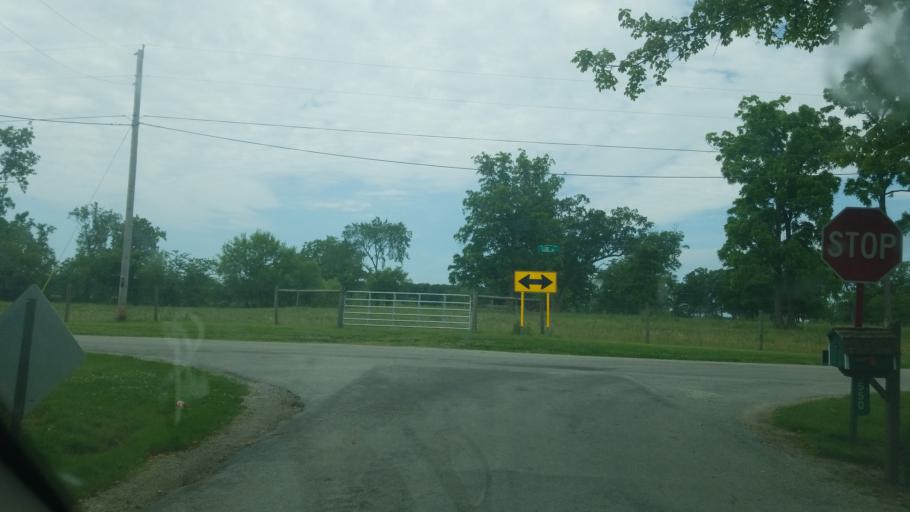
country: US
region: Ohio
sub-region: Wood County
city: North Baltimore
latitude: 41.2329
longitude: -83.6209
